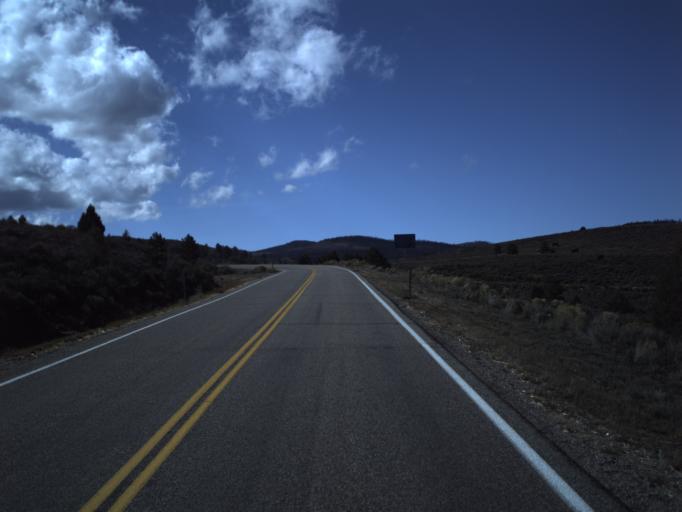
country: US
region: Utah
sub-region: Garfield County
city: Panguitch
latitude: 37.7230
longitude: -112.6223
